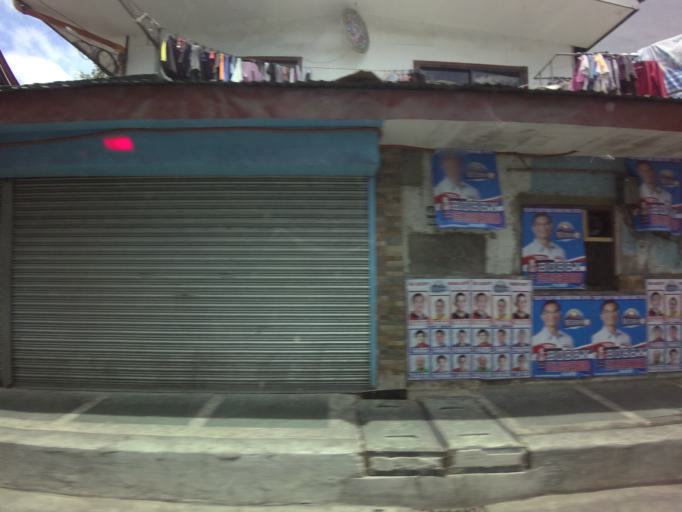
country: PH
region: Metro Manila
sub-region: Marikina
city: Calumpang
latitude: 14.6016
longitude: 121.0928
